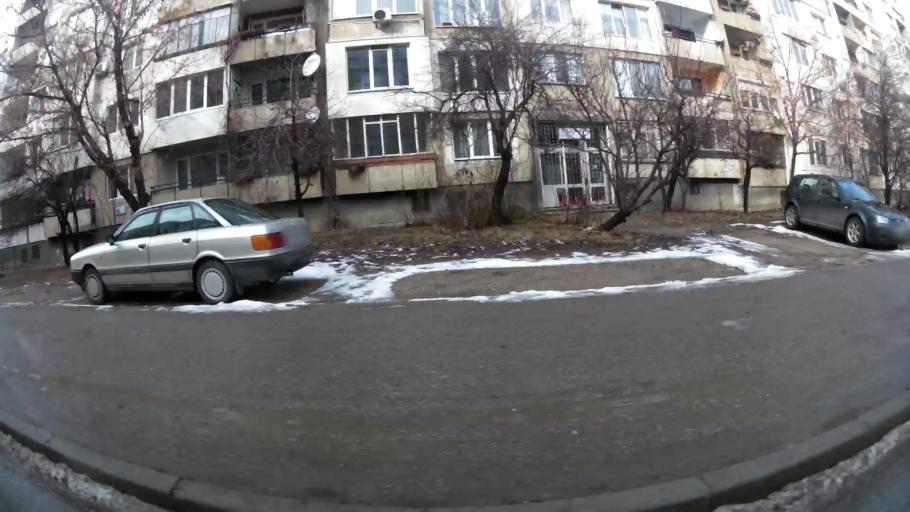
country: BG
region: Sofia-Capital
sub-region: Stolichna Obshtina
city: Sofia
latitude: 42.7136
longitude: 23.2720
